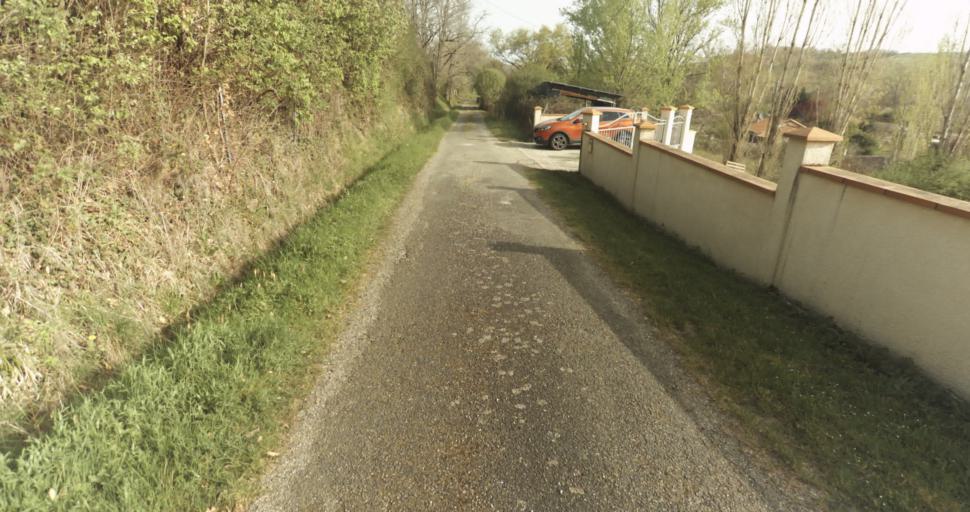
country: FR
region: Midi-Pyrenees
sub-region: Departement du Tarn-et-Garonne
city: Moissac
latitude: 44.1370
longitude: 1.1022
